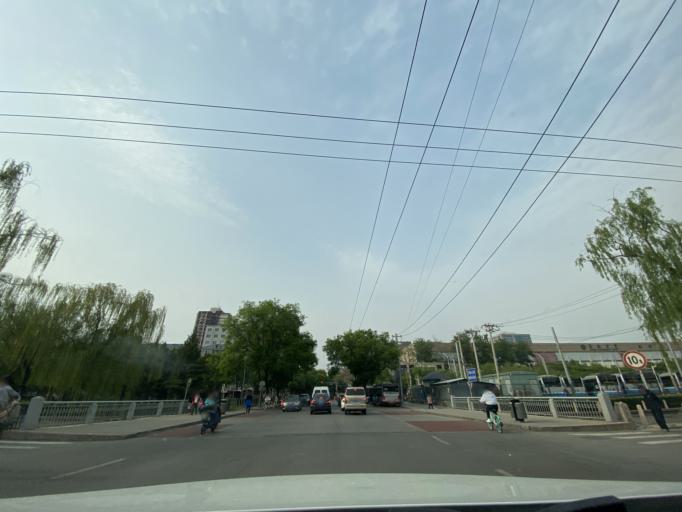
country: CN
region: Beijing
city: Datun
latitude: 39.9744
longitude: 116.3595
